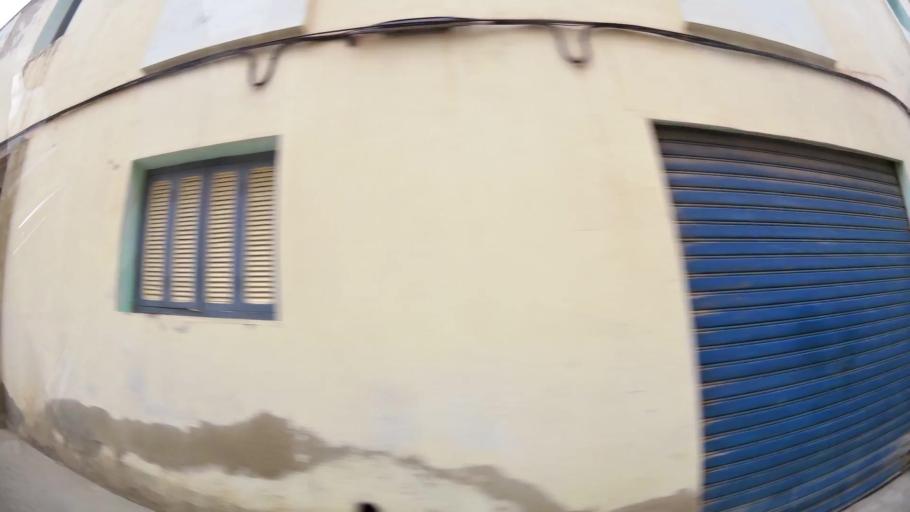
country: MA
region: Oriental
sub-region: Nador
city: Nador
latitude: 35.1649
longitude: -2.9391
